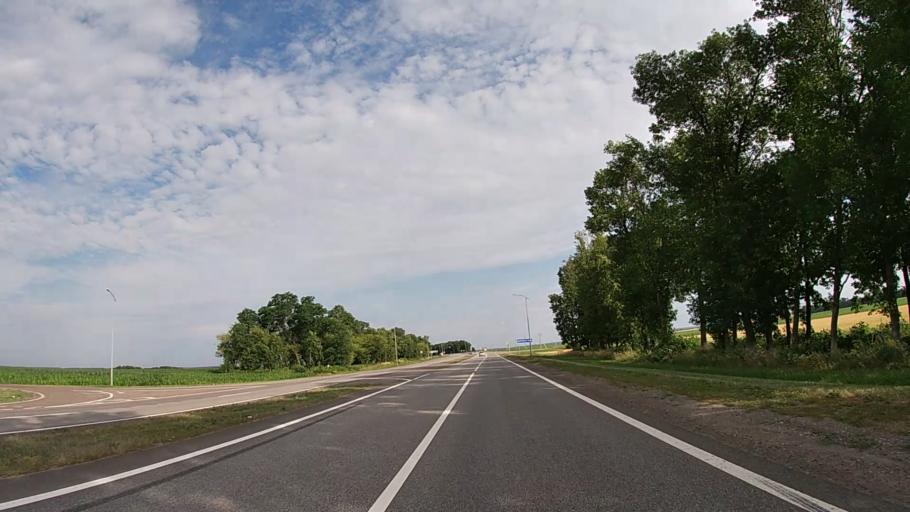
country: RU
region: Belgorod
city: Tomarovka
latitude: 50.6789
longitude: 36.2906
